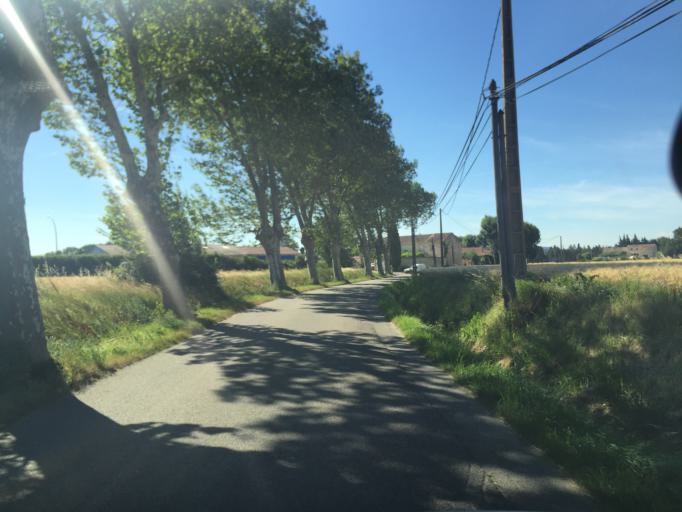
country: FR
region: Provence-Alpes-Cote d'Azur
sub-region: Departement du Vaucluse
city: Caderousse
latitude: 44.1084
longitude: 4.7460
